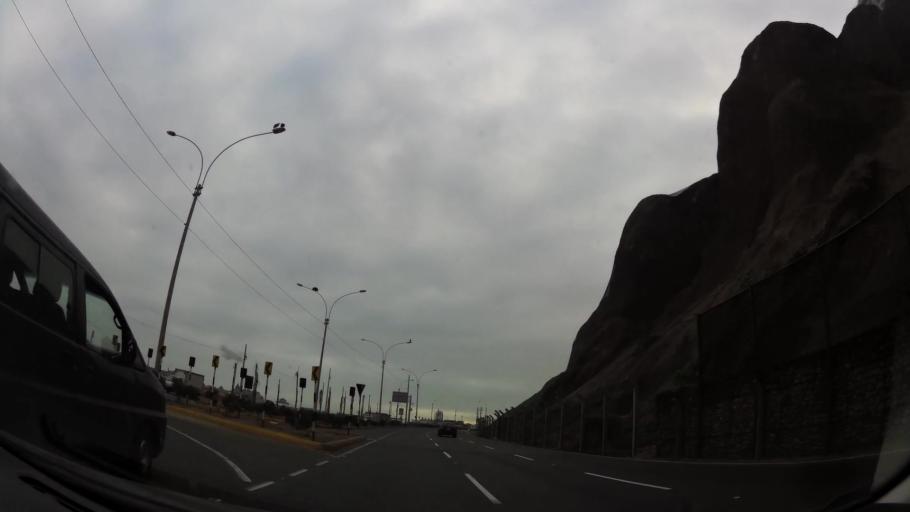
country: PE
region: Lima
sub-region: Lima
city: San Isidro
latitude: -12.1310
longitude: -77.0337
